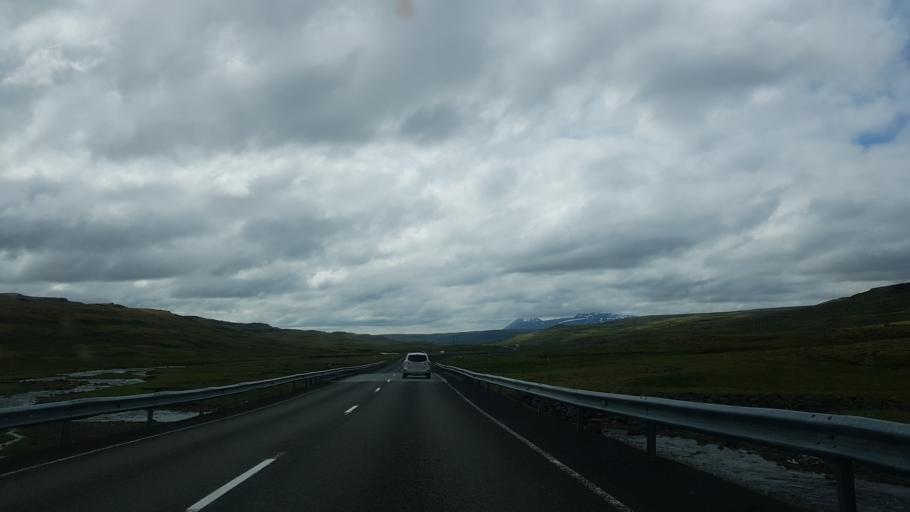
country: IS
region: West
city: Borgarnes
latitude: 64.9342
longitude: -21.0733
